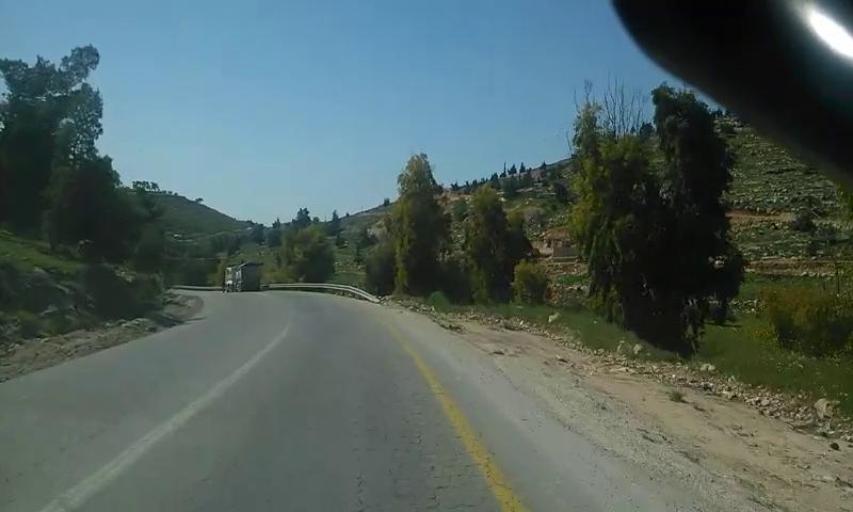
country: PS
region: West Bank
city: Ar Rihiyah
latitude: 31.4899
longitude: 35.0661
